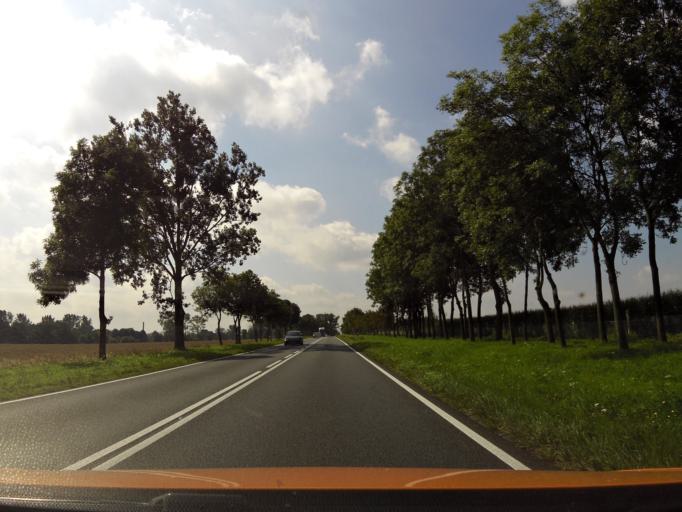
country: PL
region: West Pomeranian Voivodeship
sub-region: Powiat gryficki
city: Ploty
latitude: 53.7548
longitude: 15.2243
